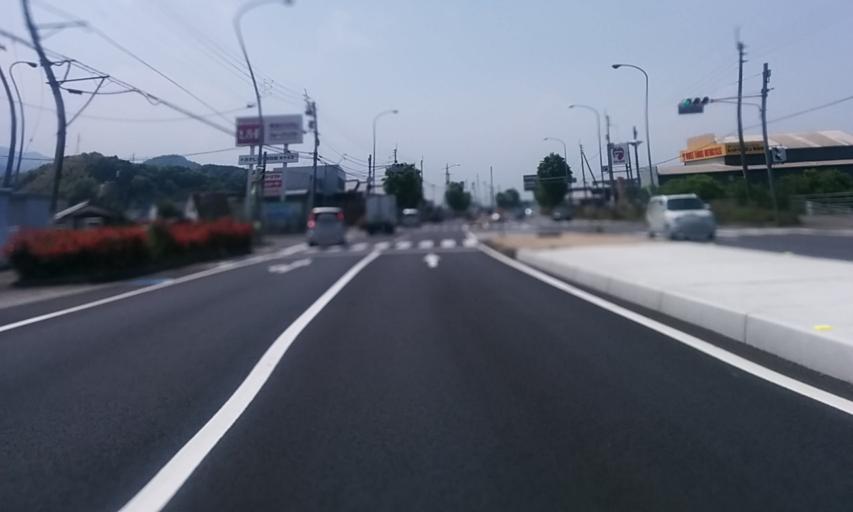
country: JP
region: Ehime
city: Niihama
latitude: 33.9215
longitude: 133.2506
